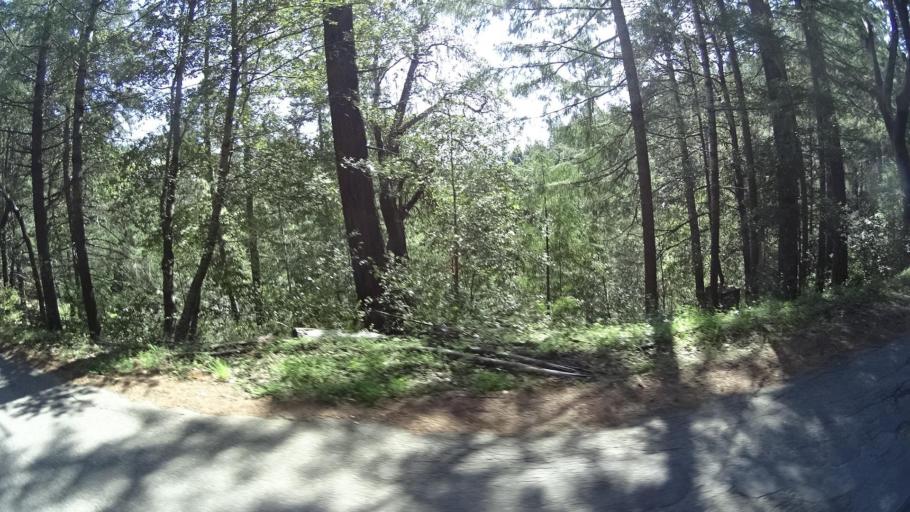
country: US
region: California
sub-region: Humboldt County
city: Redway
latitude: 40.0754
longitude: -123.6522
